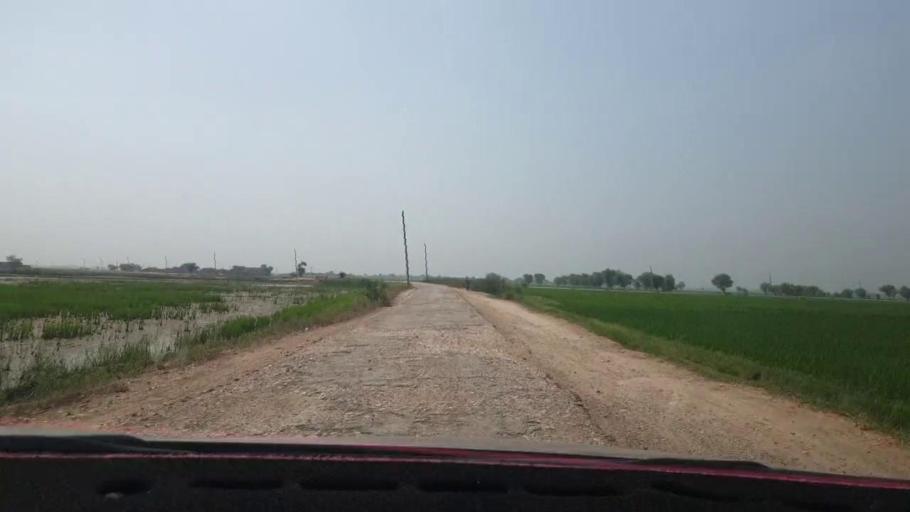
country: PK
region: Sindh
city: Warah
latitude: 27.4085
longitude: 67.8447
